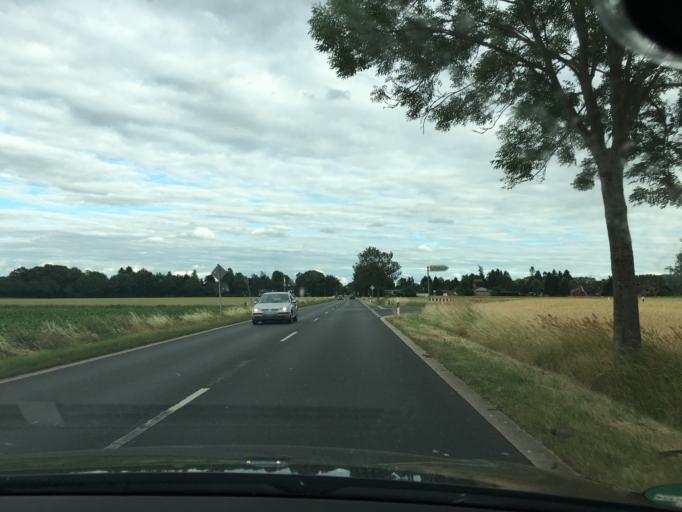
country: DE
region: North Rhine-Westphalia
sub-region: Regierungsbezirk Koln
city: Dueren
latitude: 50.7798
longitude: 6.4498
